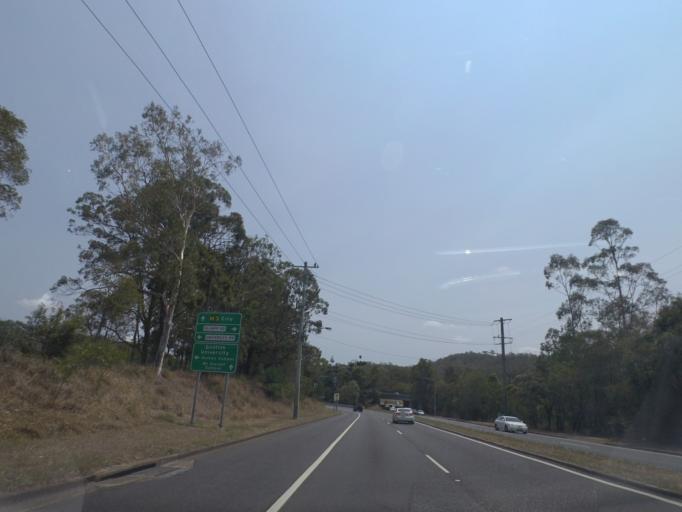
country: AU
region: Queensland
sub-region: Brisbane
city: Nathan
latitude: -27.5533
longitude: 153.0675
